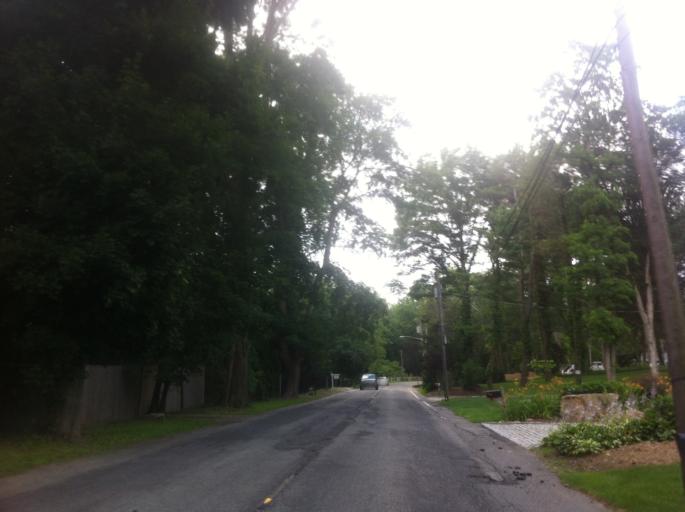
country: US
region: New York
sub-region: Nassau County
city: Locust Valley
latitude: 40.8546
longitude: -73.5920
